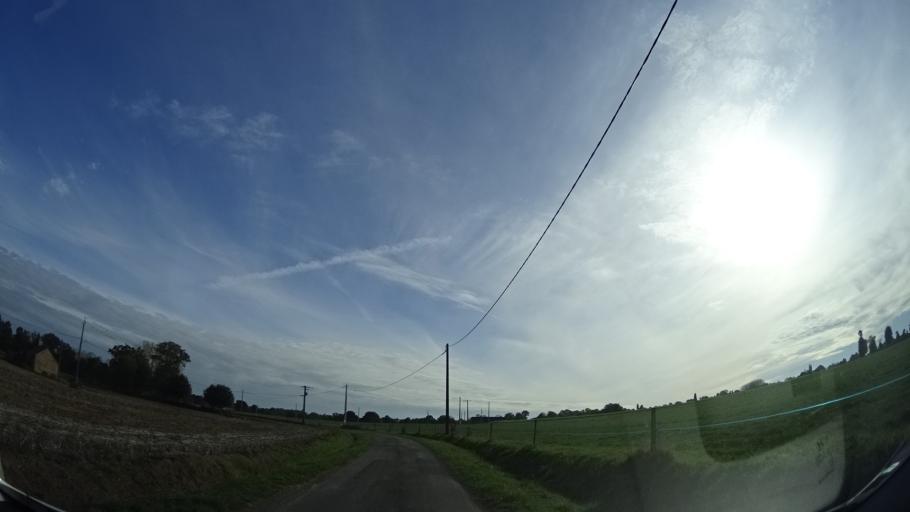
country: FR
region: Brittany
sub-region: Departement d'Ille-et-Vilaine
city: Geveze
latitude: 48.2400
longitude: -1.8298
